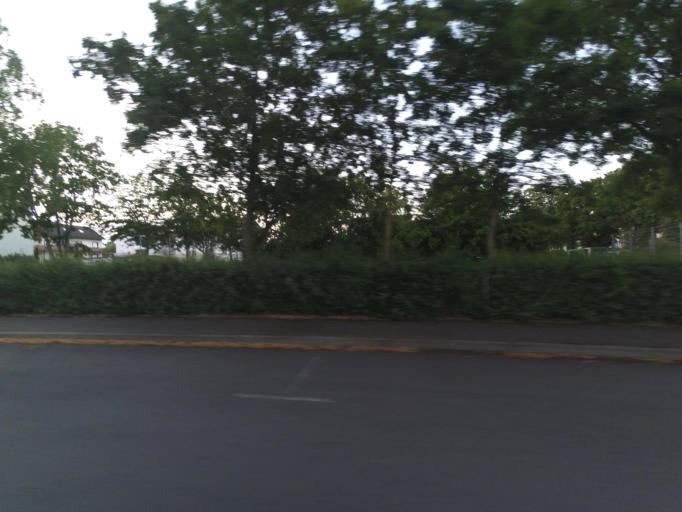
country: DE
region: Bavaria
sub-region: Regierungsbezirk Unterfranken
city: Hassfurt
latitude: 50.0385
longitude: 10.5188
